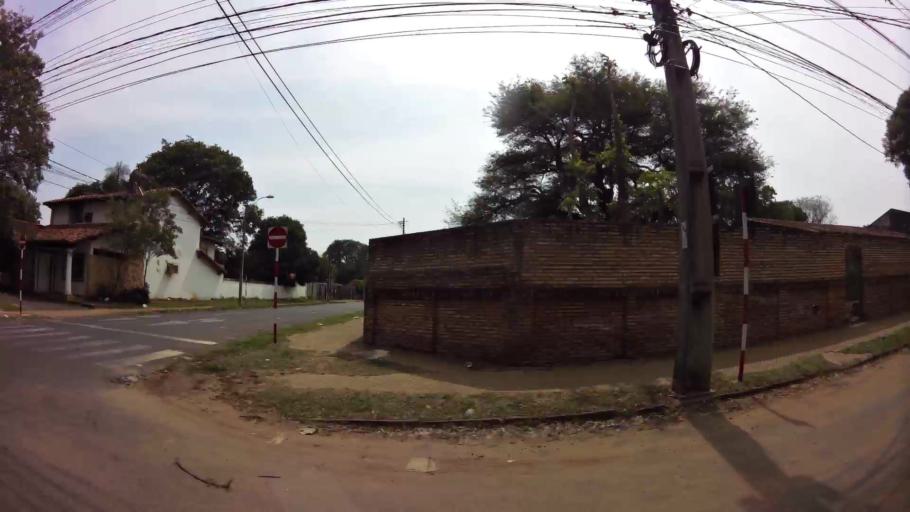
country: PY
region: Asuncion
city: Asuncion
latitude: -25.2821
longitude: -57.5693
